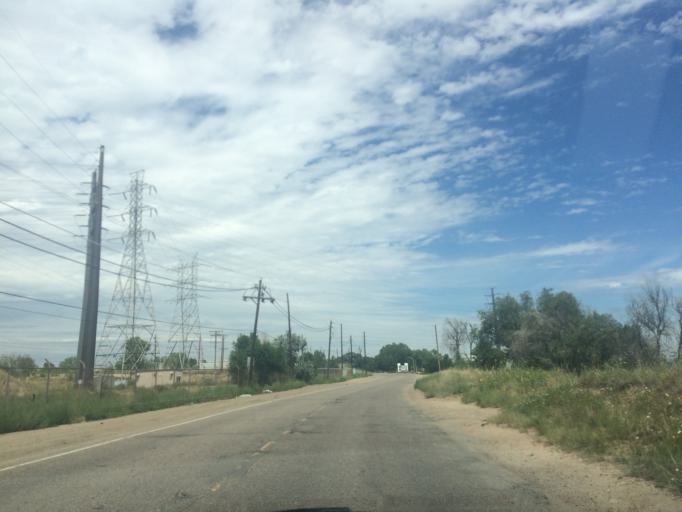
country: US
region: Colorado
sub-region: Adams County
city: Welby
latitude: 39.8109
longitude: -104.9599
